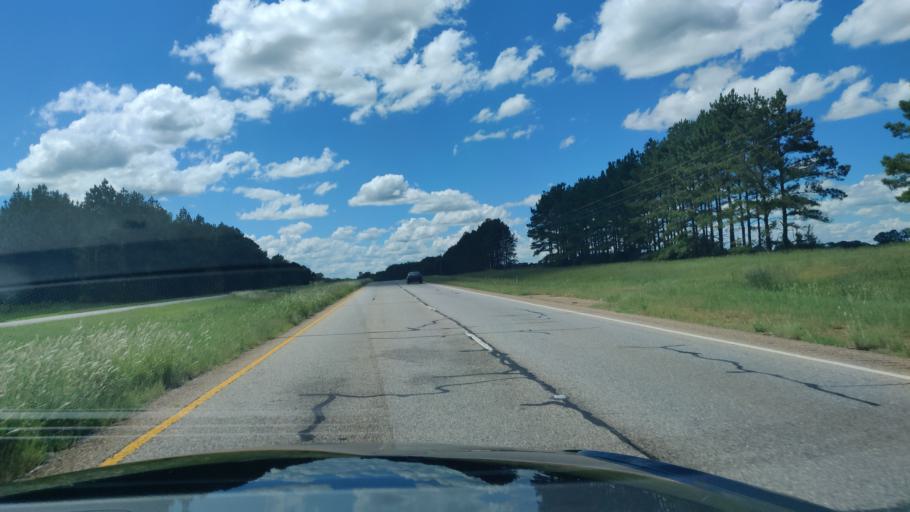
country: US
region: Georgia
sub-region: Webster County
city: Preston
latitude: 31.9624
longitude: -84.5955
